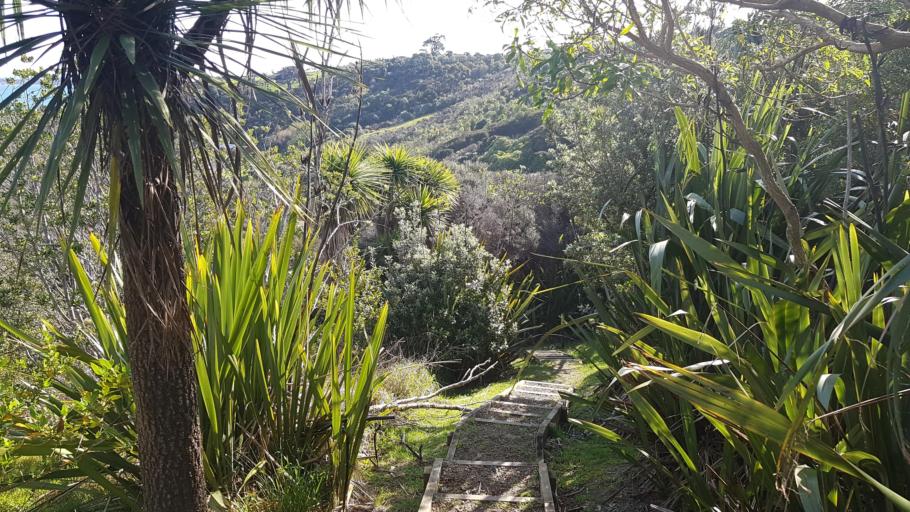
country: NZ
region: Auckland
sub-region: Auckland
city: Pakuranga
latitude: -36.7763
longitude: 174.9942
